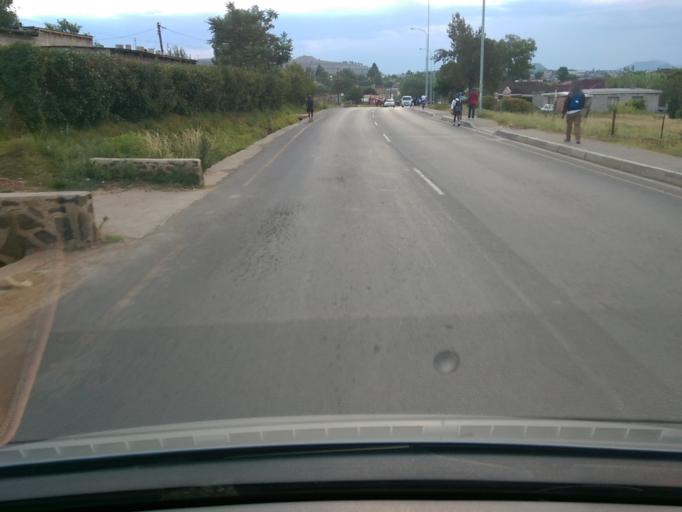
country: LS
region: Maseru
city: Maseru
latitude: -29.3094
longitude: 27.5276
